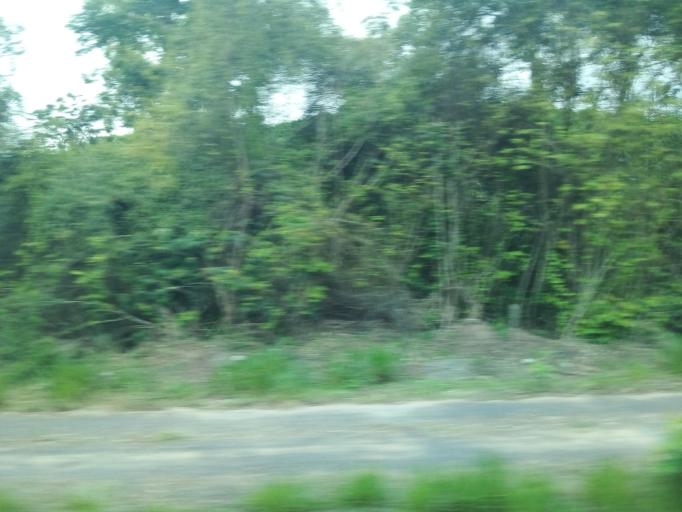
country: BR
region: Minas Gerais
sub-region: Rio Piracicaba
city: Rio Piracicaba
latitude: -19.9460
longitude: -43.1796
